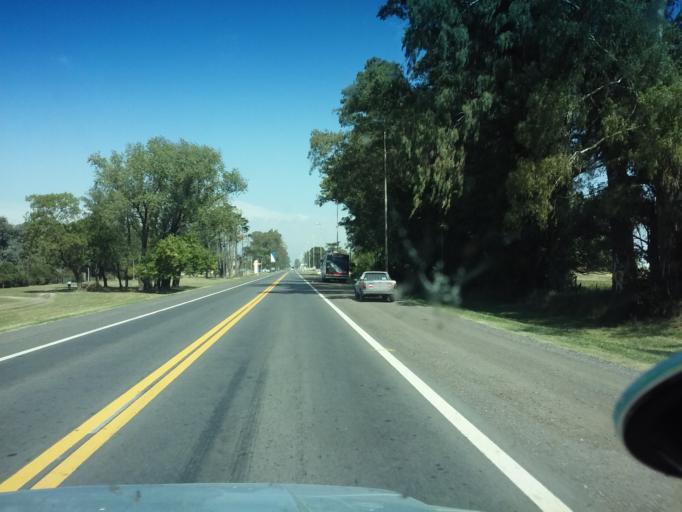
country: AR
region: Buenos Aires
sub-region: Partido de Nueve de Julio
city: Nueve de Julio
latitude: -35.4784
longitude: -60.8696
